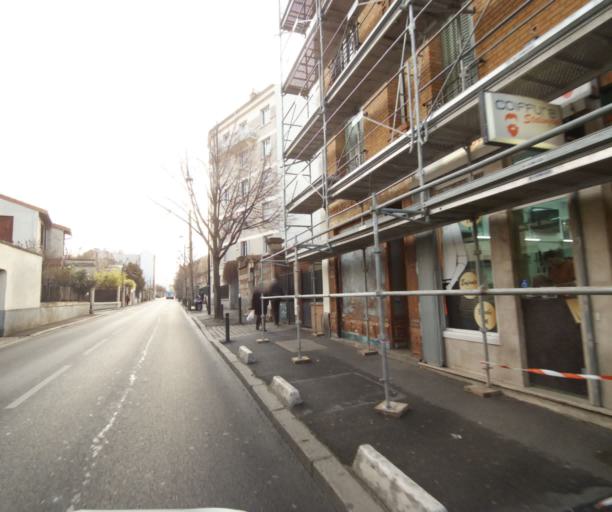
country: FR
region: Ile-de-France
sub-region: Departement des Hauts-de-Seine
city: Nanterre
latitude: 48.8940
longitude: 2.1962
